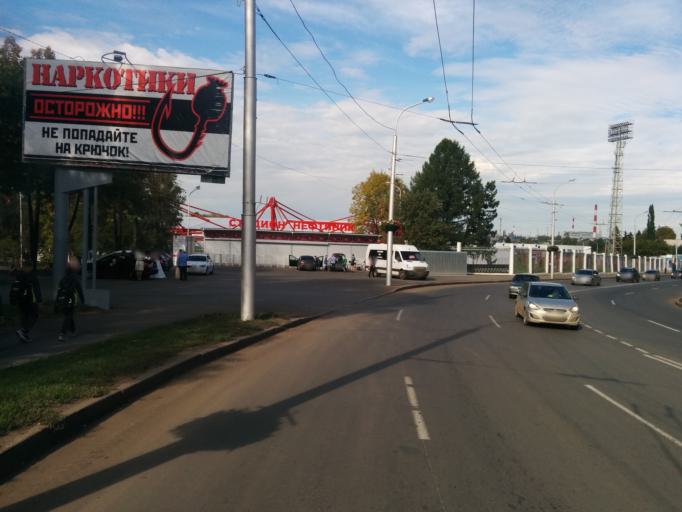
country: RU
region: Bashkortostan
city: Ufa
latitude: 54.8240
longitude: 56.0603
